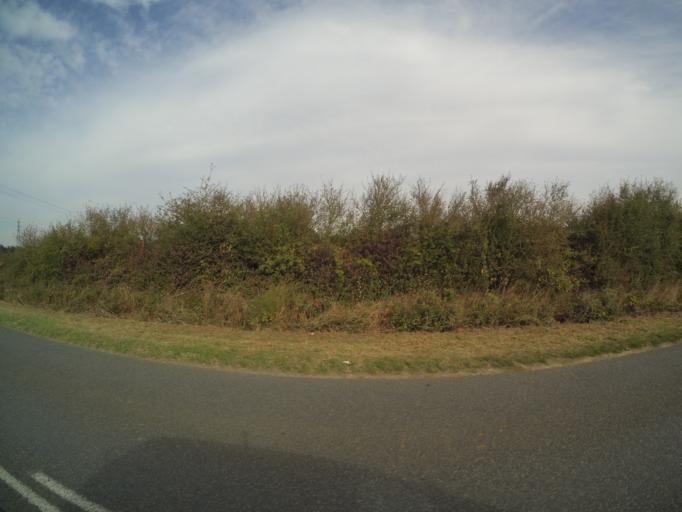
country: FR
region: Pays de la Loire
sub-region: Departement de Maine-et-Loire
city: Chemille-Melay
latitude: 47.2114
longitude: -0.7503
